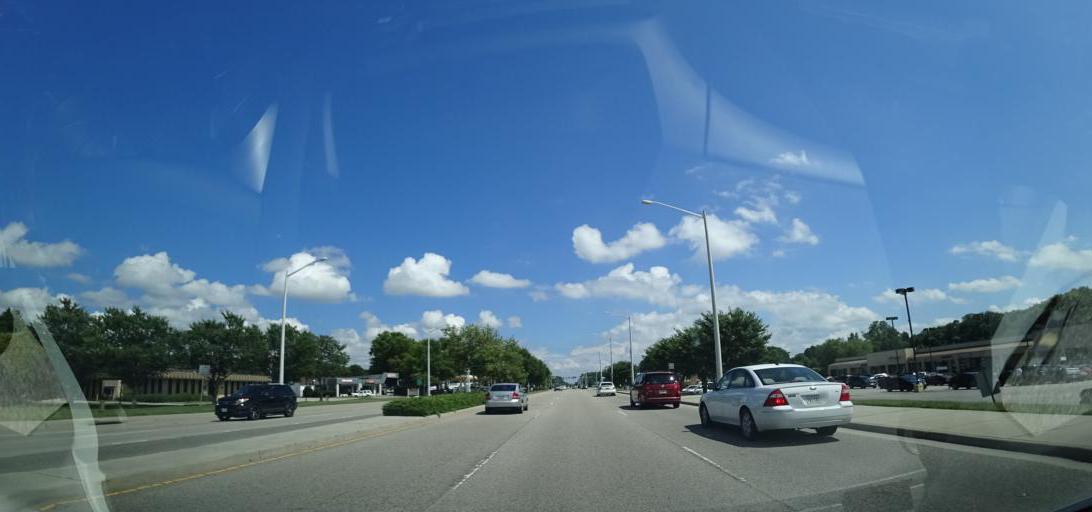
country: US
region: Virginia
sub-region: York County
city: Yorktown
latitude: 37.1509
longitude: -76.5298
